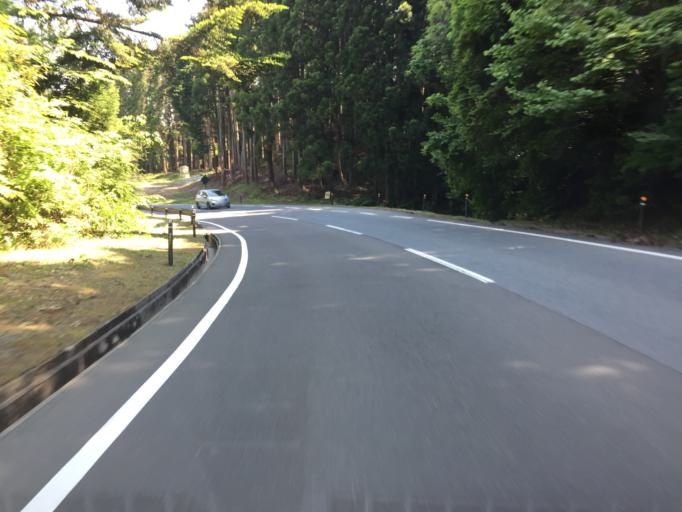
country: JP
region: Miyagi
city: Marumori
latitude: 37.7932
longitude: 140.8823
